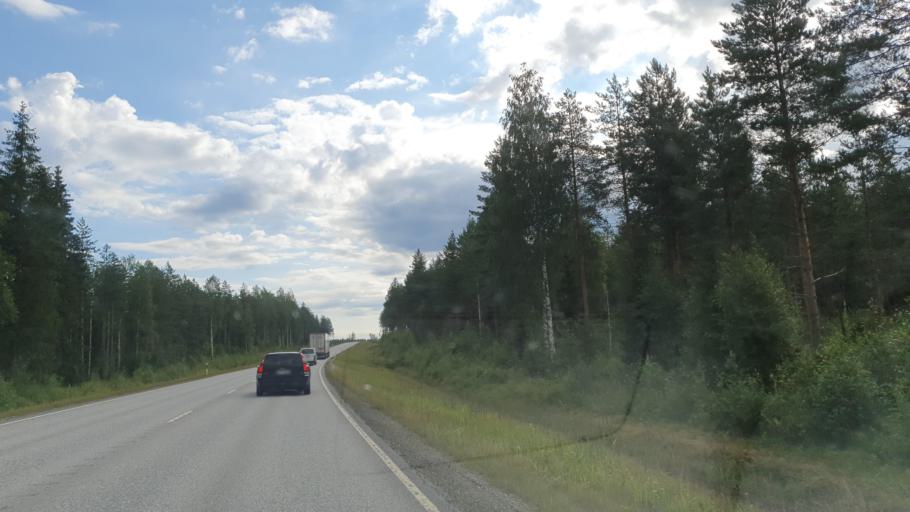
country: FI
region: Central Finland
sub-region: Jyvaeskylae
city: Hankasalmi
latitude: 62.3910
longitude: 26.6201
